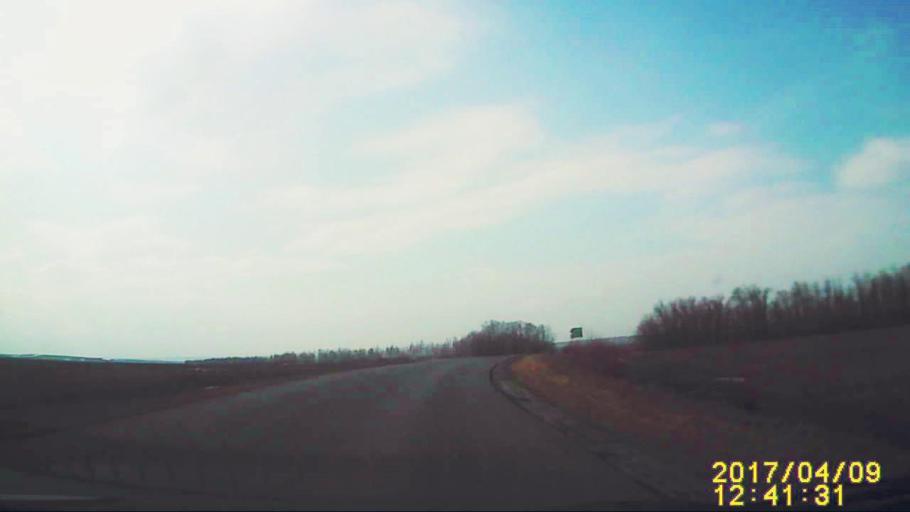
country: RU
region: Ulyanovsk
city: Ignatovka
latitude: 54.0009
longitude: 47.9363
